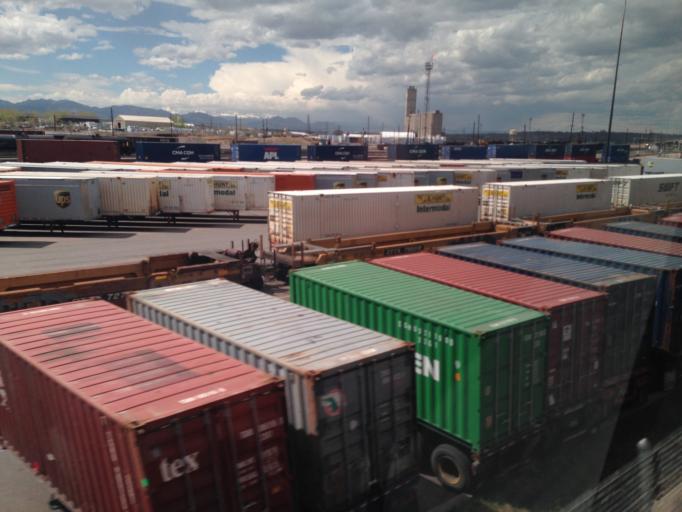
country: US
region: Colorado
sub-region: Adams County
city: Twin Lakes
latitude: 39.7962
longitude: -104.9966
